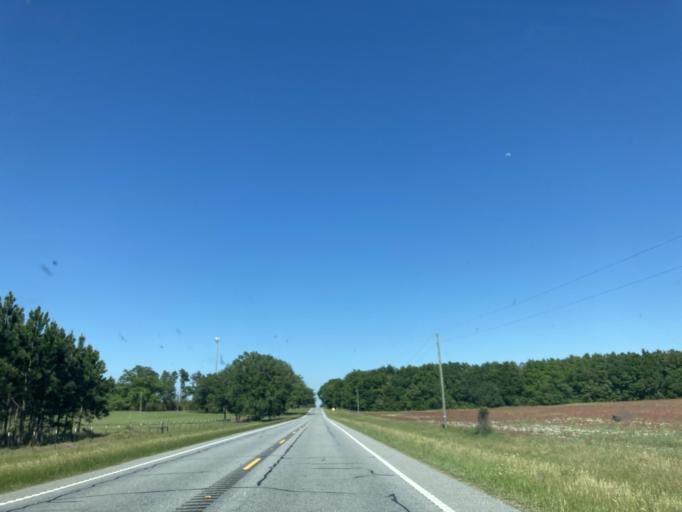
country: US
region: Georgia
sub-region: Baker County
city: Newton
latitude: 31.2673
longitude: -84.3969
